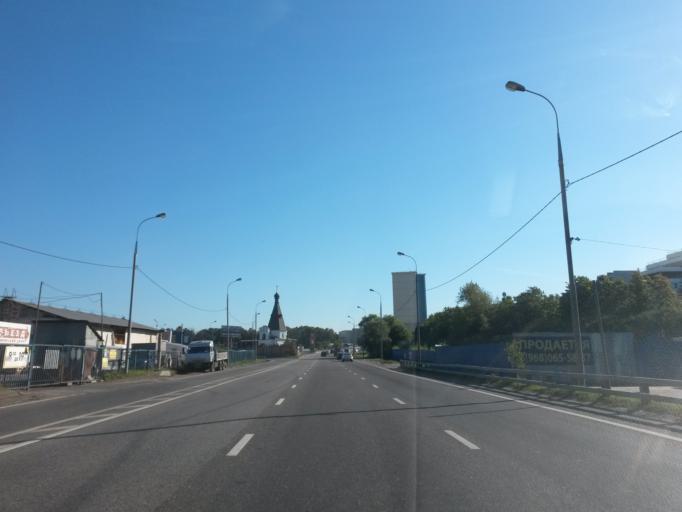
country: RU
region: Moscow
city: Annino
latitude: 55.5732
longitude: 37.6023
